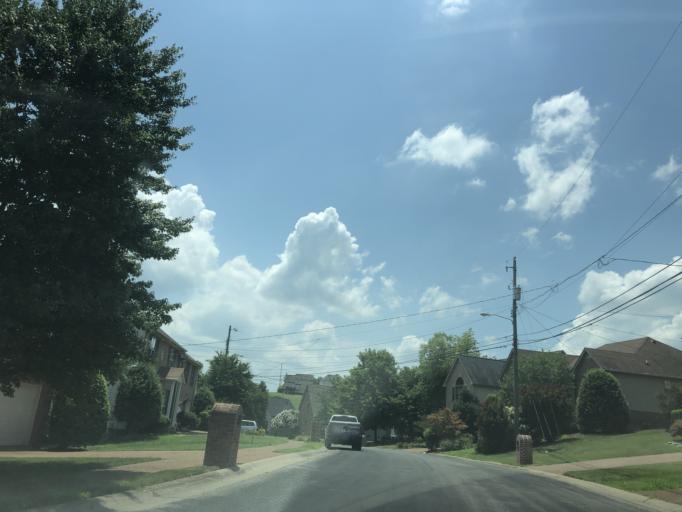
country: US
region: Tennessee
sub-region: Williamson County
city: Brentwood Estates
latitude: 36.0211
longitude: -86.7252
